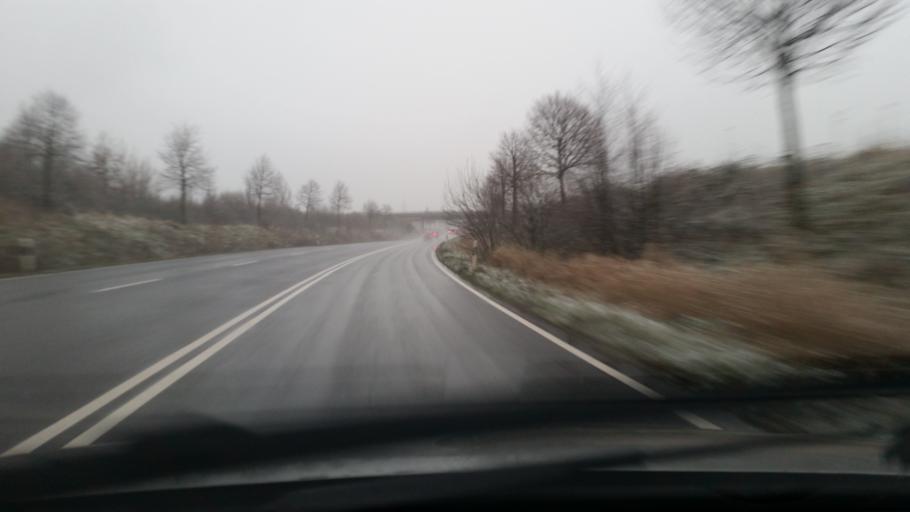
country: DE
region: Lower Saxony
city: Gehrden
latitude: 52.2795
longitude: 9.6251
